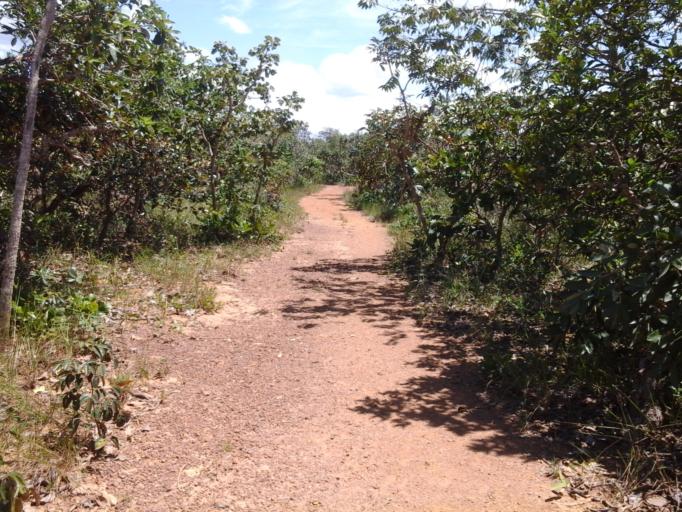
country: BR
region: Goias
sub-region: Abadiania
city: Abadiania
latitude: -15.9767
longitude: -48.5330
